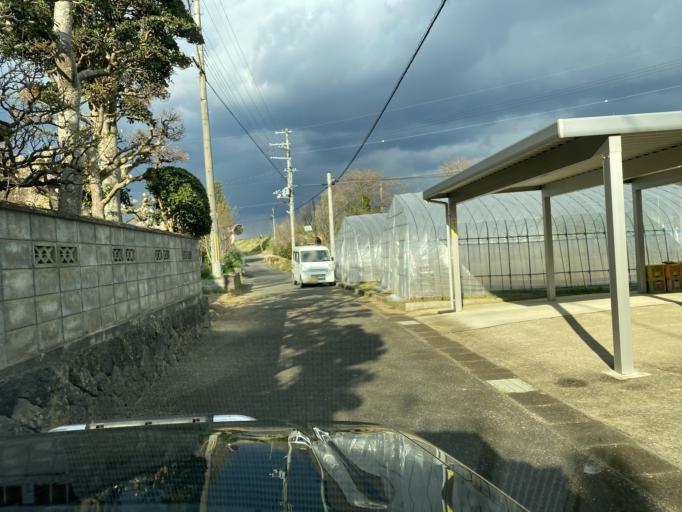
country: JP
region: Hyogo
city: Toyooka
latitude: 35.4943
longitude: 134.8067
